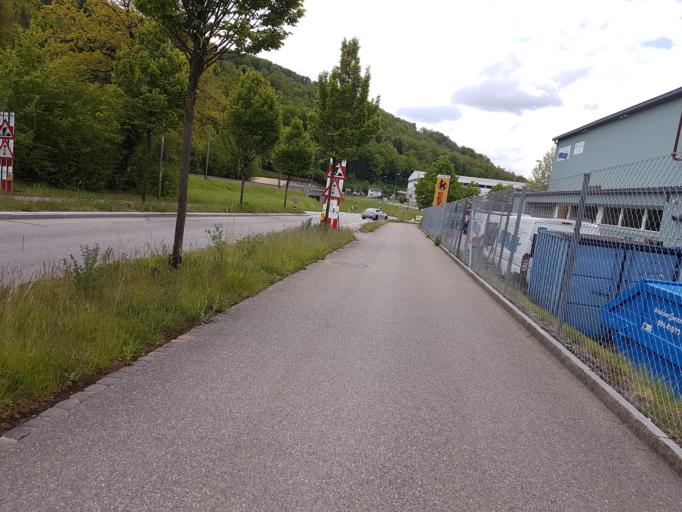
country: CH
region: Aargau
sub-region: Bezirk Brugg
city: Hausen
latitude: 47.4699
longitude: 8.1902
